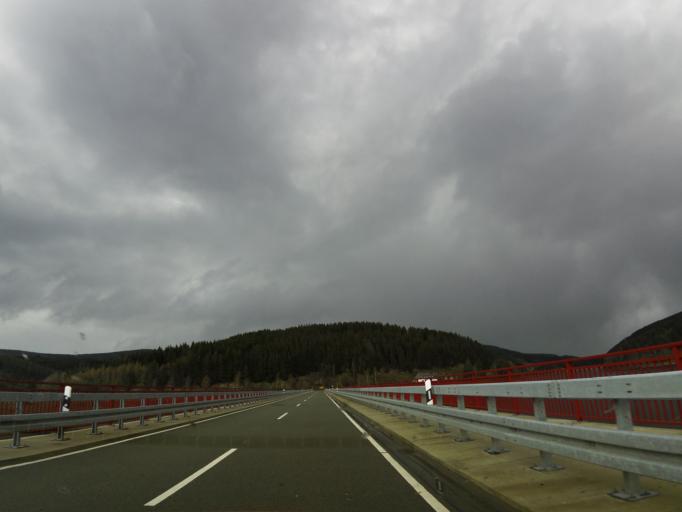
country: DE
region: Lower Saxony
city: Schulenberg im Oberharz
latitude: 51.8396
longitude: 10.4506
